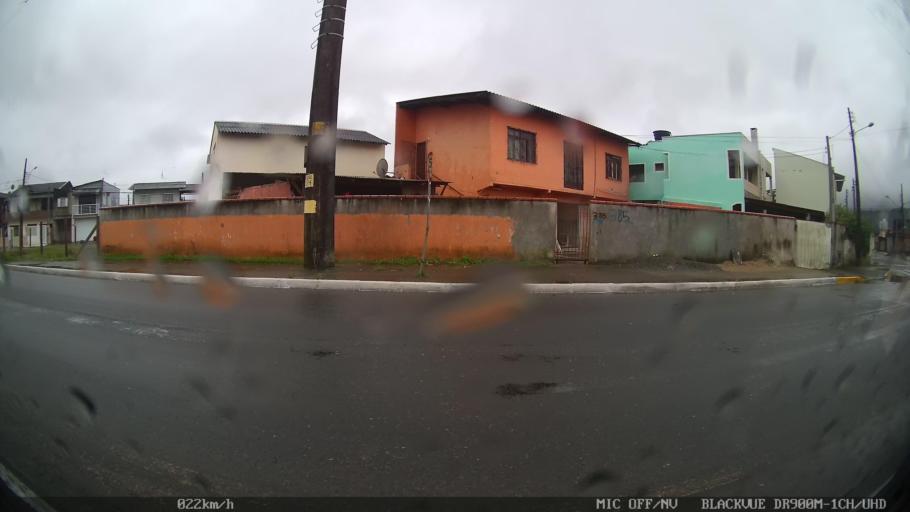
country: BR
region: Santa Catarina
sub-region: Itajai
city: Itajai
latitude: -26.9233
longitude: -48.6969
